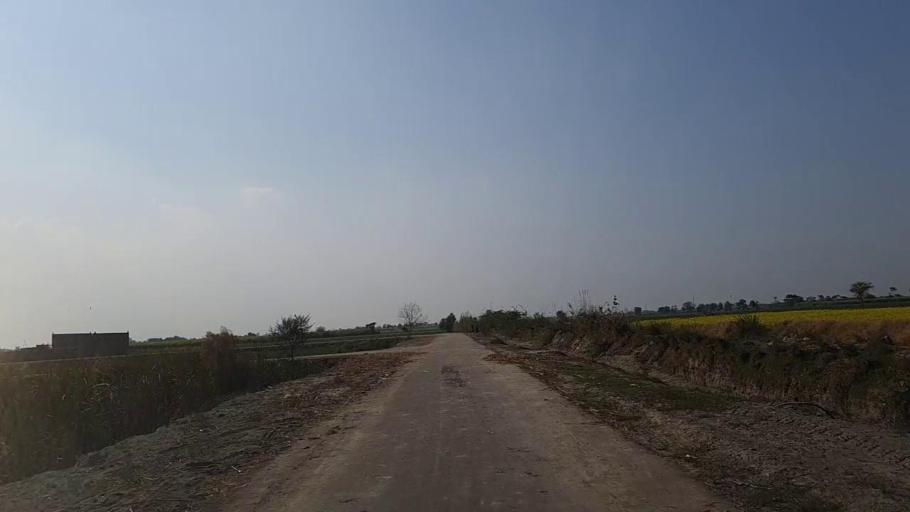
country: PK
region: Sindh
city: Jam Sahib
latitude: 26.3002
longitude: 68.5710
